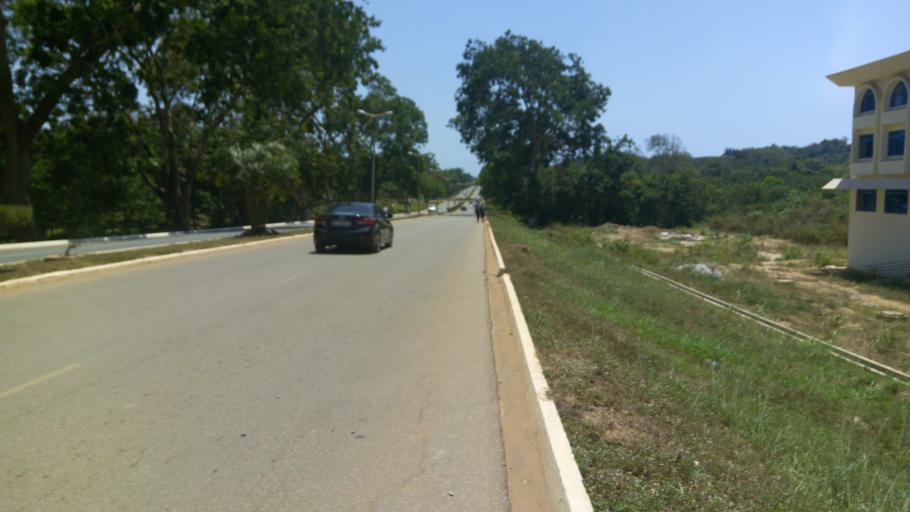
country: GH
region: Central
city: Cape Coast
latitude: 5.1160
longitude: -1.2909
